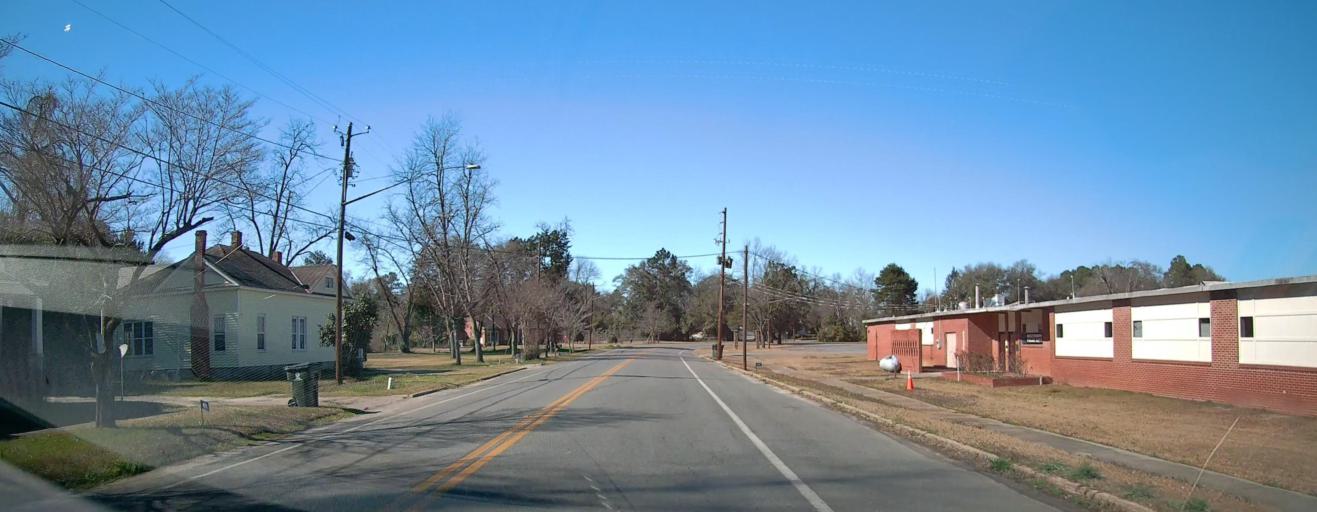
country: US
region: Georgia
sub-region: Macon County
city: Oglethorpe
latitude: 32.2982
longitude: -84.0648
